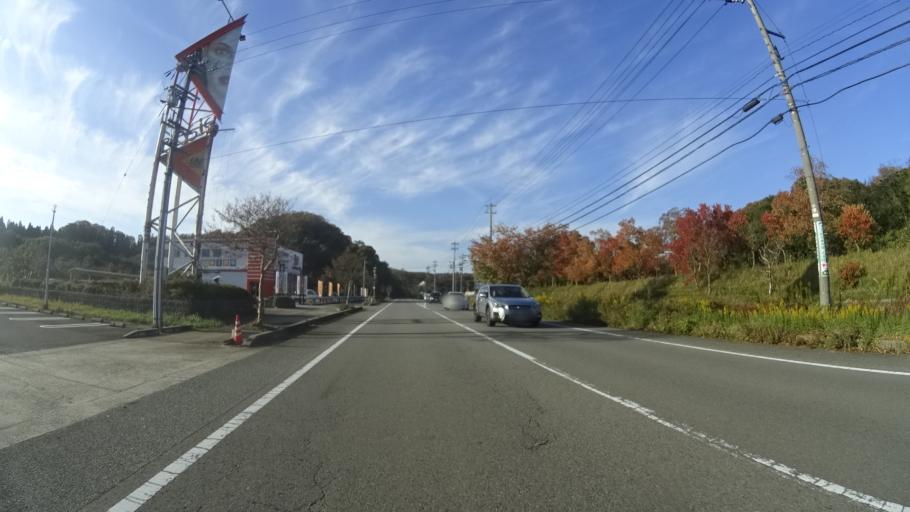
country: JP
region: Ishikawa
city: Hakui
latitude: 37.0263
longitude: 136.7830
